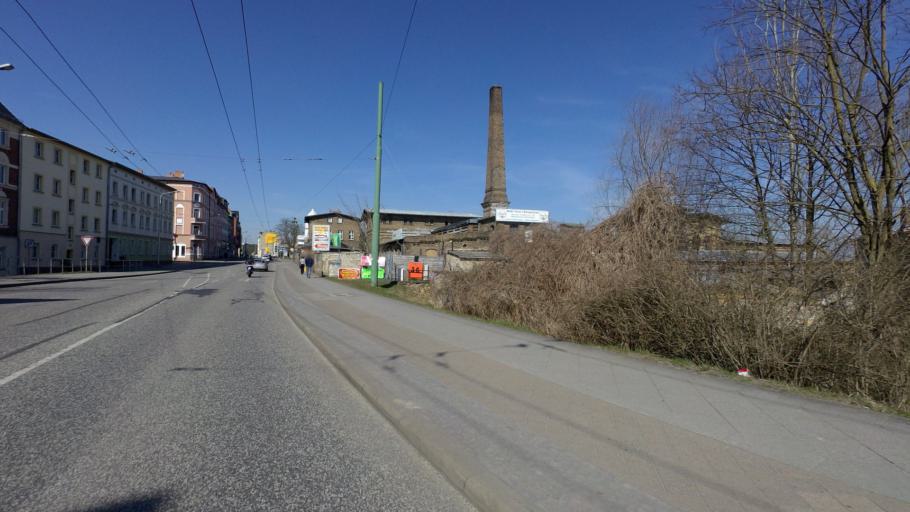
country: DE
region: Brandenburg
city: Eberswalde
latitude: 52.8364
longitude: 13.8195
